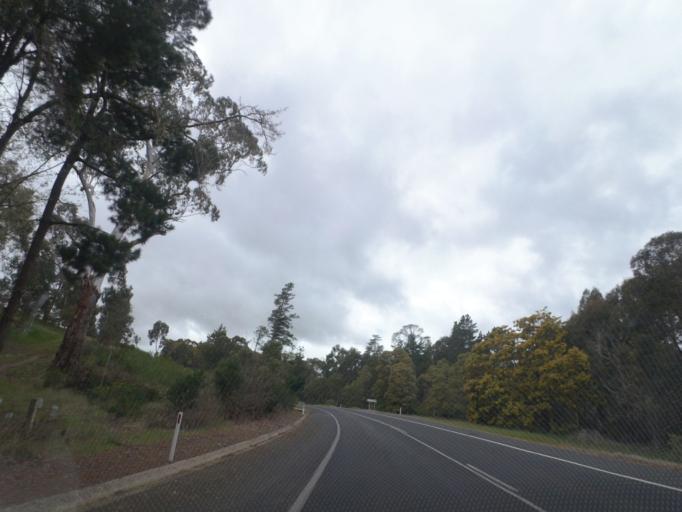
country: AU
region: Victoria
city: Brown Hill
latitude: -37.4186
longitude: 143.9012
